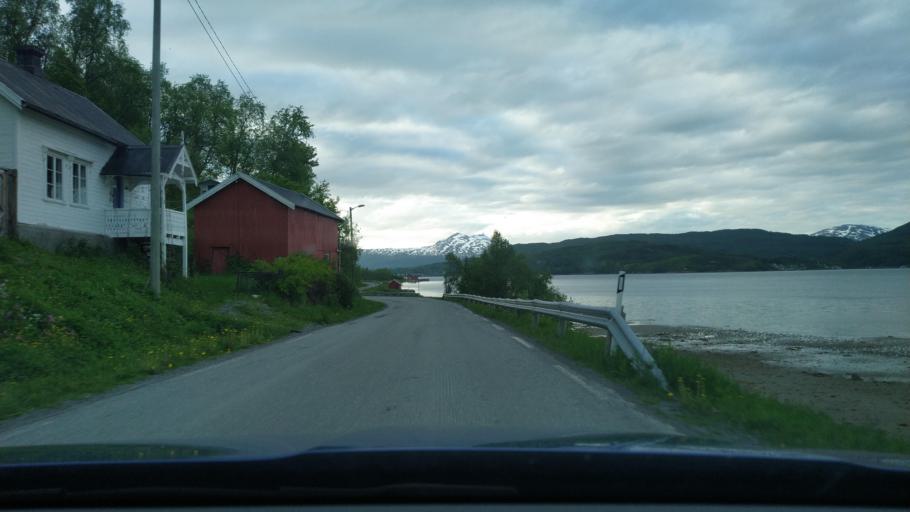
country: NO
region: Troms
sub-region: Sorreisa
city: Sorreisa
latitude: 69.1386
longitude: 18.0578
